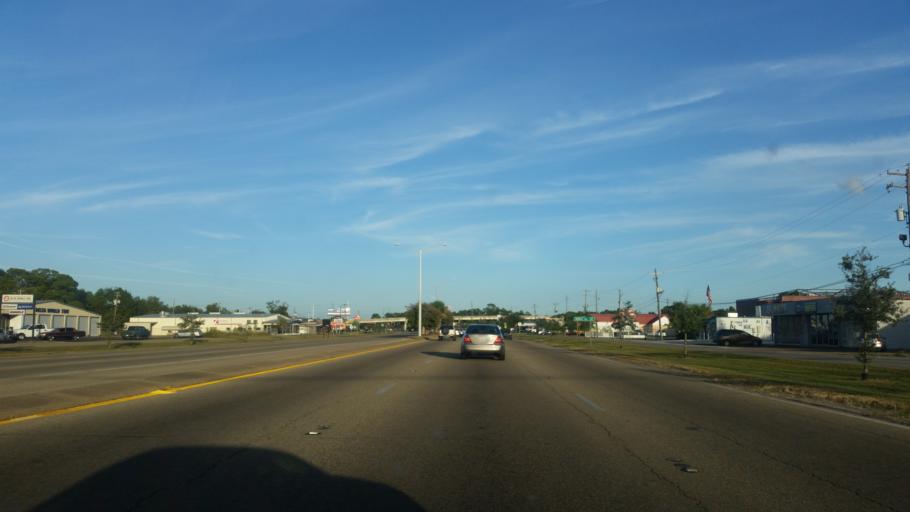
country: US
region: Mississippi
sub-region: Jackson County
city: Pascagoula
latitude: 30.3708
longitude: -88.5444
